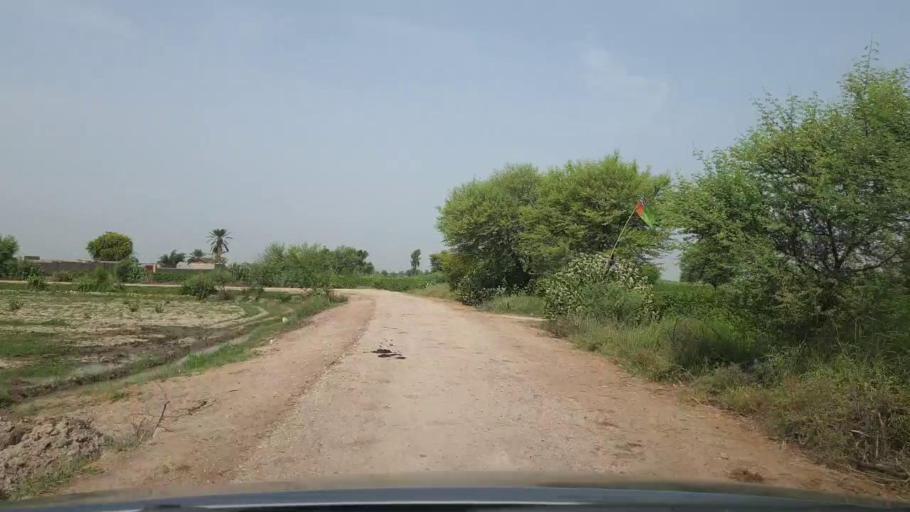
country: PK
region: Sindh
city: Rohri
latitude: 27.6554
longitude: 69.0110
